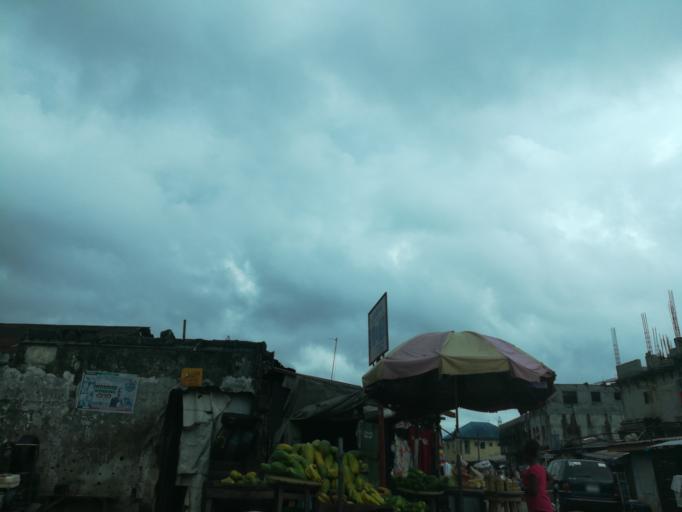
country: NG
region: Rivers
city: Port Harcourt
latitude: 4.8357
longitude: 7.0311
